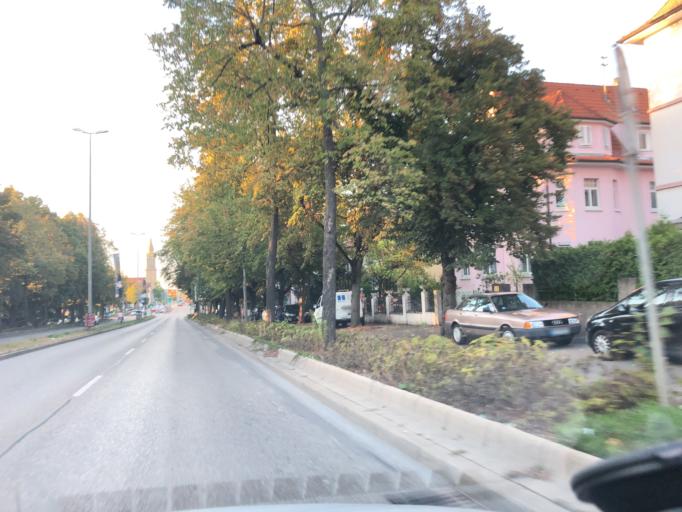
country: DE
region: Baden-Wuerttemberg
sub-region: Regierungsbezirk Stuttgart
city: Ludwigsburg
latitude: 48.8861
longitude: 9.1946
